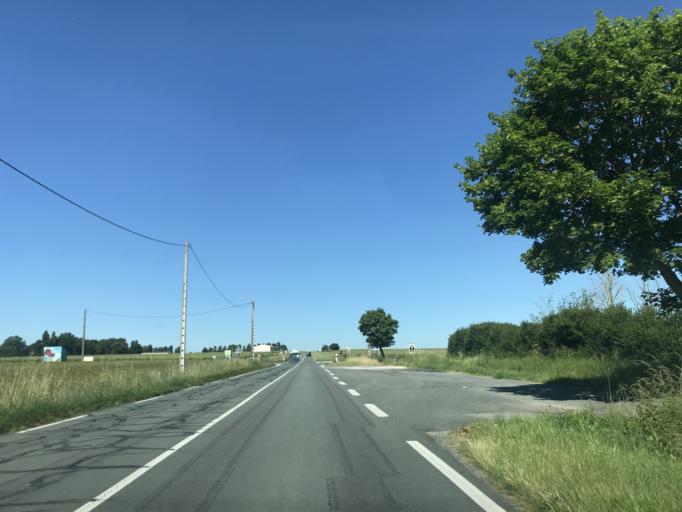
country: FR
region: Poitou-Charentes
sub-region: Departement de la Charente-Maritime
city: Perignac
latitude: 45.5756
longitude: -0.4831
